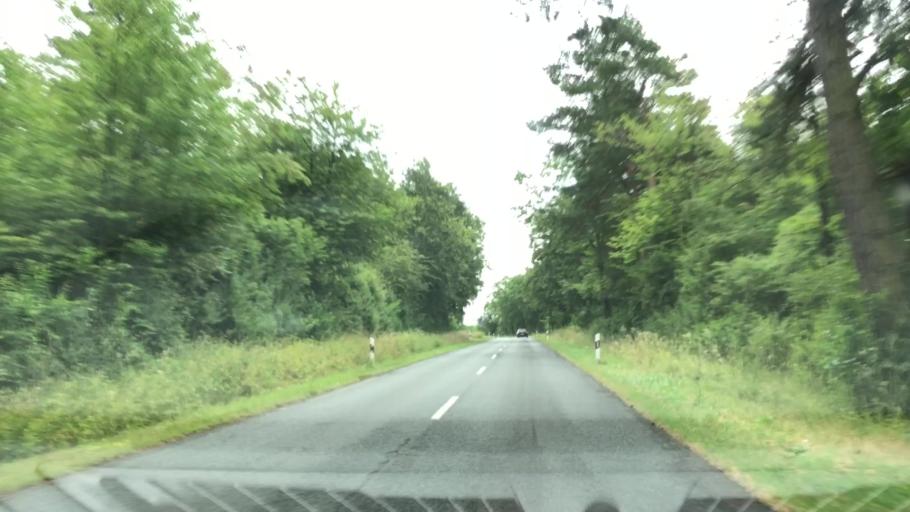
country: DE
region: Hesse
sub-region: Regierungsbezirk Darmstadt
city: Steinau an der Strasse
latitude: 50.3011
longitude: 9.4838
